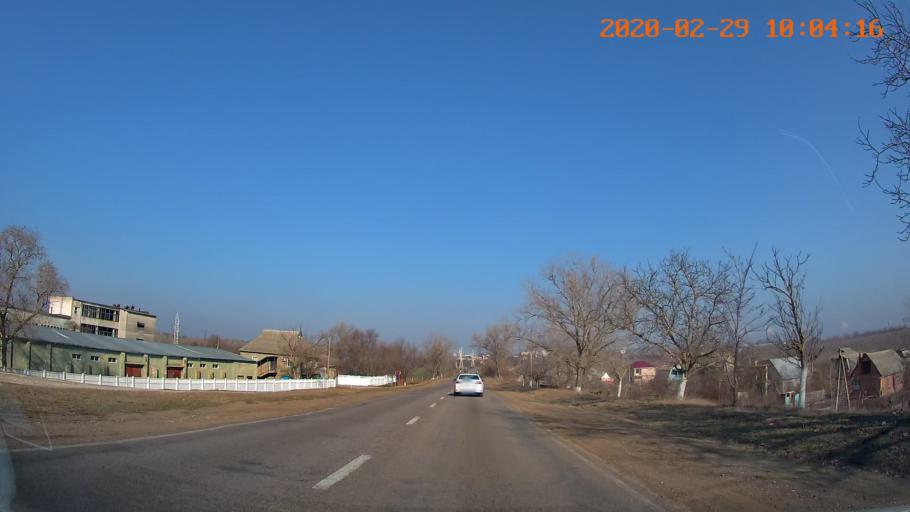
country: MD
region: Causeni
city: Chitcani
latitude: 46.7968
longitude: 29.6764
